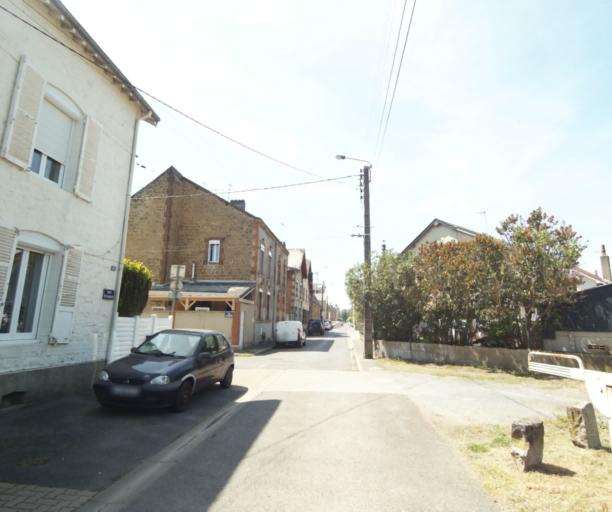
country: FR
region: Champagne-Ardenne
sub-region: Departement des Ardennes
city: Charleville-Mezieres
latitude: 49.7634
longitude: 4.7246
